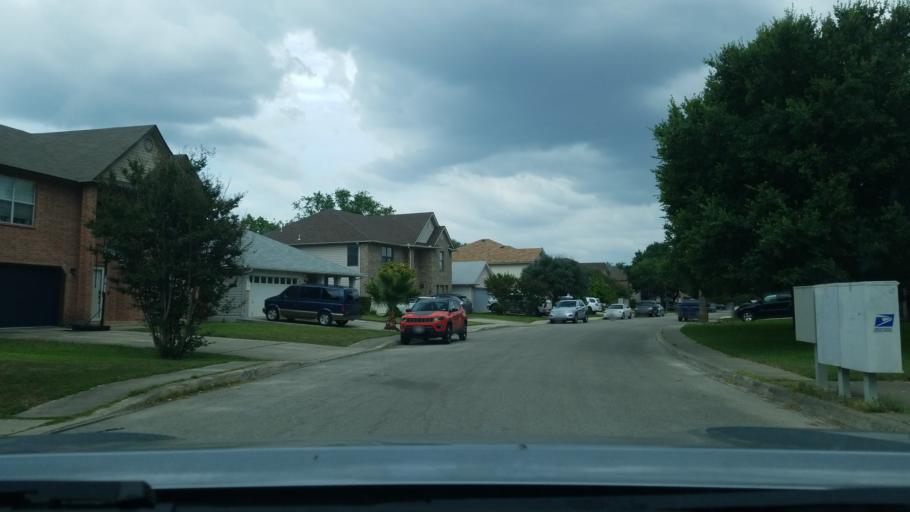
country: US
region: Texas
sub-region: Bexar County
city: Leon Valley
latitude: 29.5418
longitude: -98.6279
